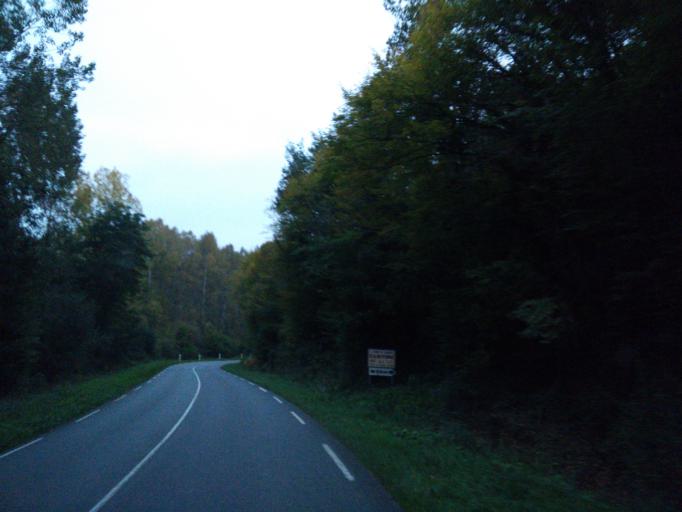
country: FR
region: Aquitaine
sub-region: Departement de la Dordogne
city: Sarlat-la-Caneda
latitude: 44.9068
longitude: 1.1383
